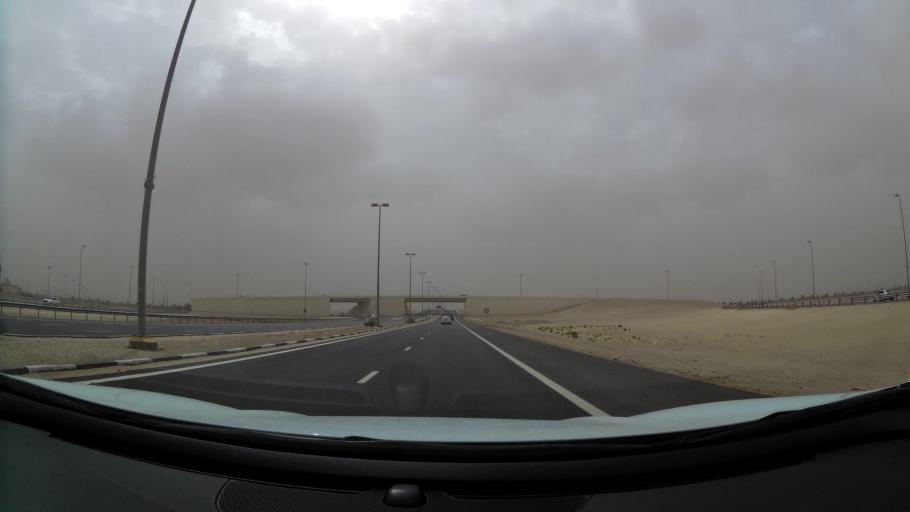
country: AE
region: Abu Dhabi
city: Abu Dhabi
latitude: 24.4193
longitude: 54.7137
